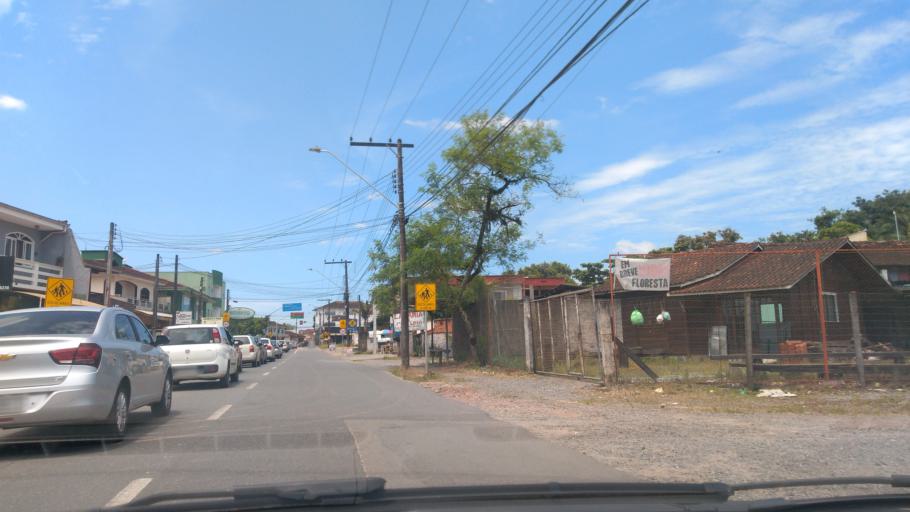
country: BR
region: Santa Catarina
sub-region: Joinville
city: Joinville
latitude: -26.3250
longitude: -48.8104
